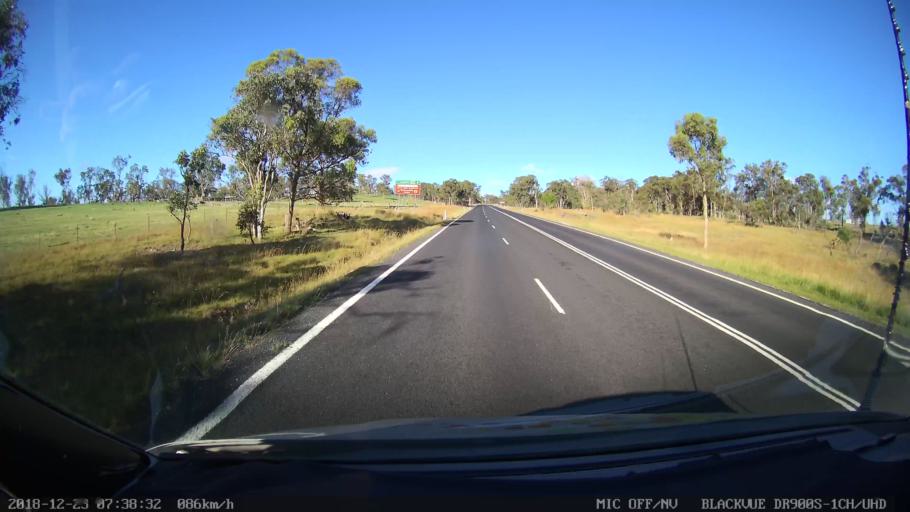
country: AU
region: New South Wales
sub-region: Armidale Dumaresq
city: Enmore
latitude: -30.5190
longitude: 152.0326
